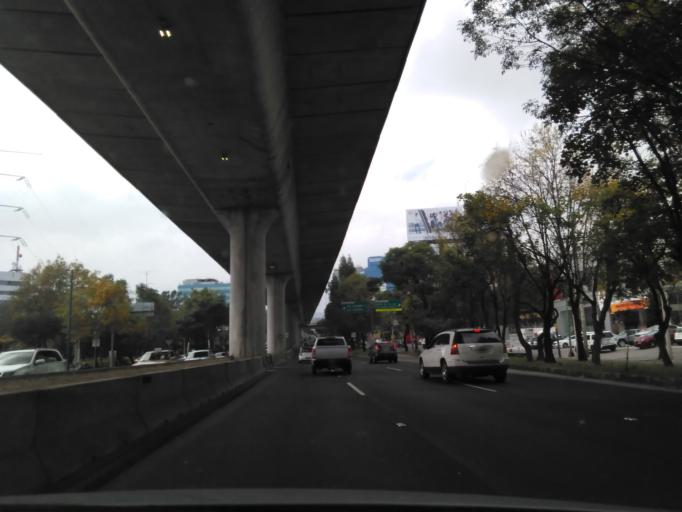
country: MX
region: Mexico City
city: Magdalena Contreras
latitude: 19.3059
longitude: -99.2067
